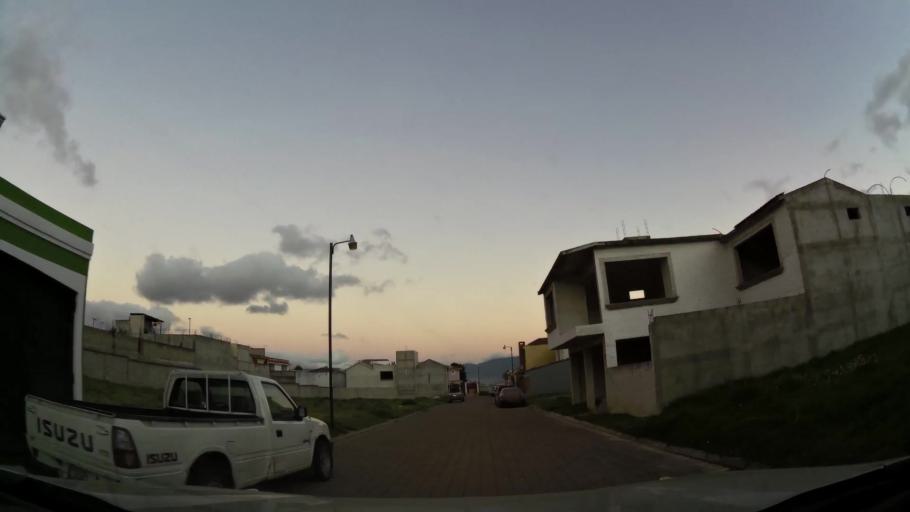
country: GT
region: Quetzaltenango
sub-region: Municipio de La Esperanza
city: La Esperanza
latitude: 14.8636
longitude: -91.5449
